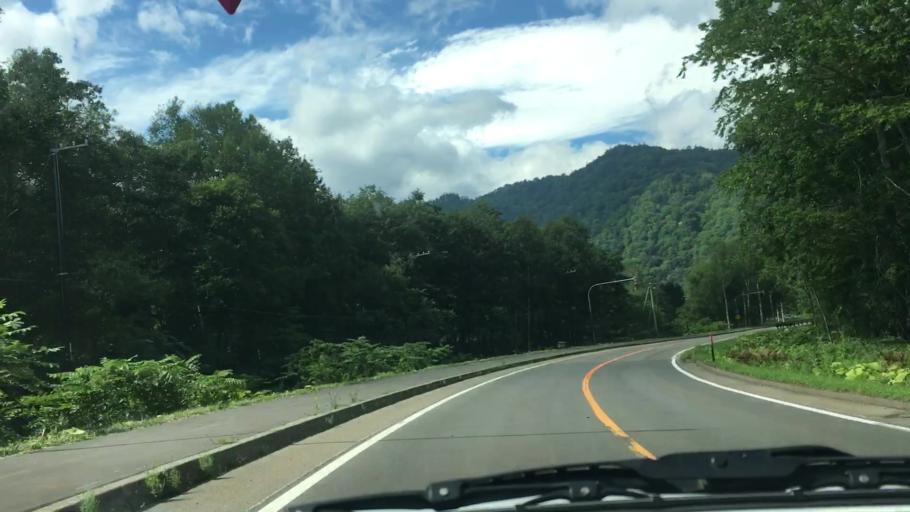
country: JP
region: Hokkaido
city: Otofuke
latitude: 43.3565
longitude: 143.2555
